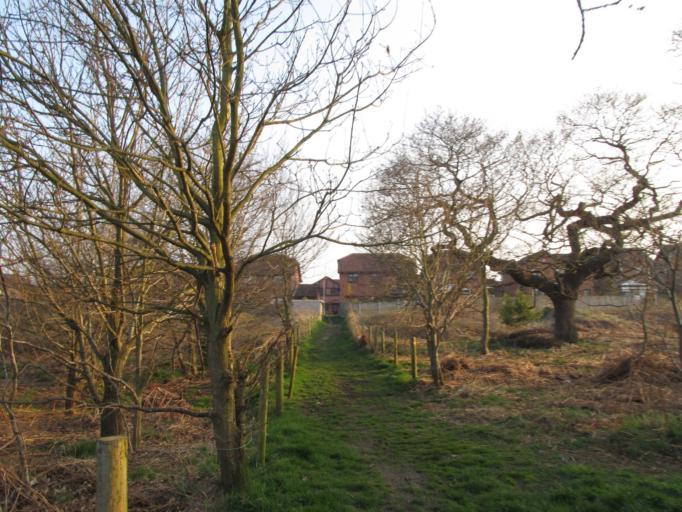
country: GB
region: Wales
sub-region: County of Flintshire
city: Buckley
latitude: 53.2036
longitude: -3.0903
